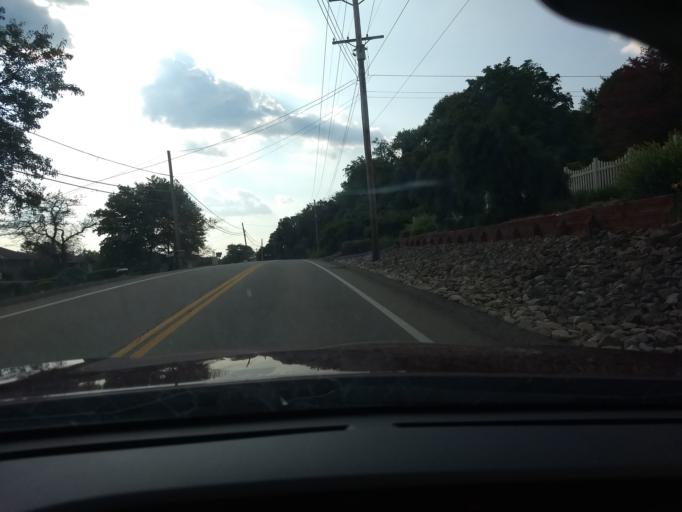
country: US
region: Pennsylvania
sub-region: Allegheny County
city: Curtisville
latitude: 40.6327
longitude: -79.8679
